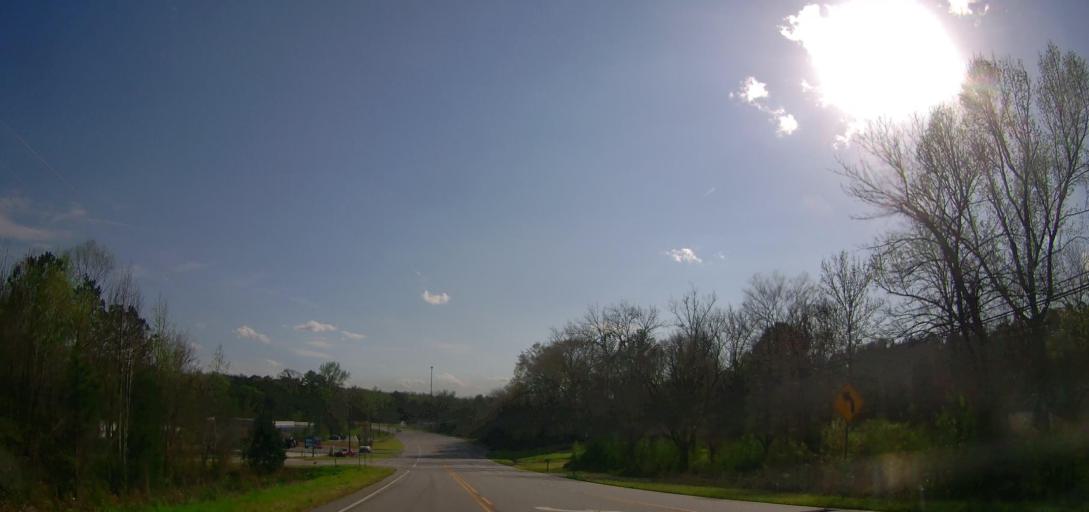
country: US
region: Georgia
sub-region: Baldwin County
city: Hardwick
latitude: 33.0401
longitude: -83.2341
